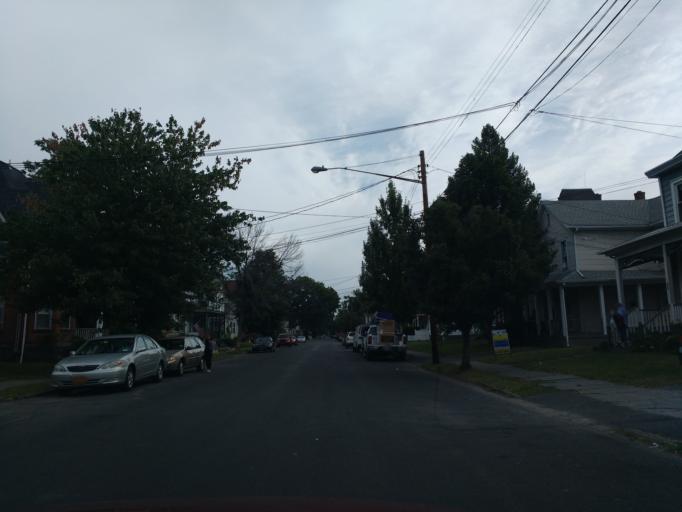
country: US
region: New York
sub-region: Ulster County
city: Kingston
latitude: 41.9330
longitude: -74.0048
